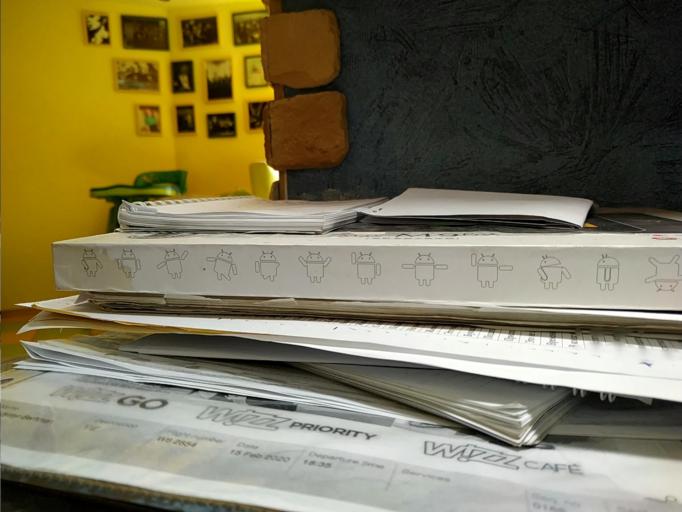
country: RU
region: Novgorod
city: Sol'tsy
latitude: 58.1100
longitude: 30.0969
